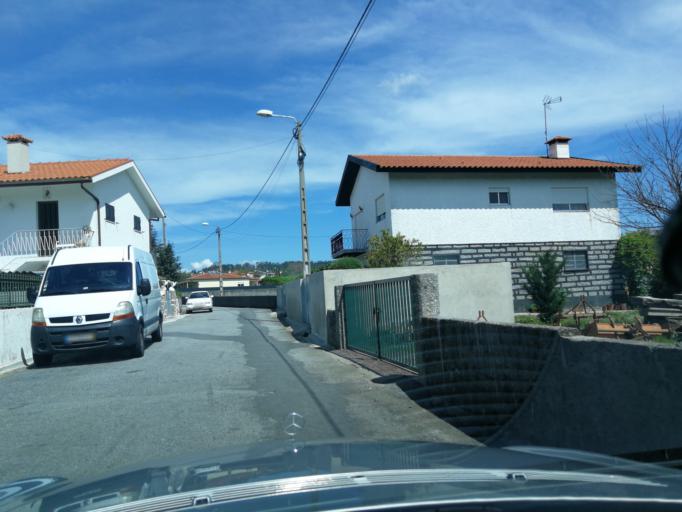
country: PT
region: Braga
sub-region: Vila Nova de Famalicao
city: Vila Nova de Famalicao
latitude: 41.4312
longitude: -8.5279
